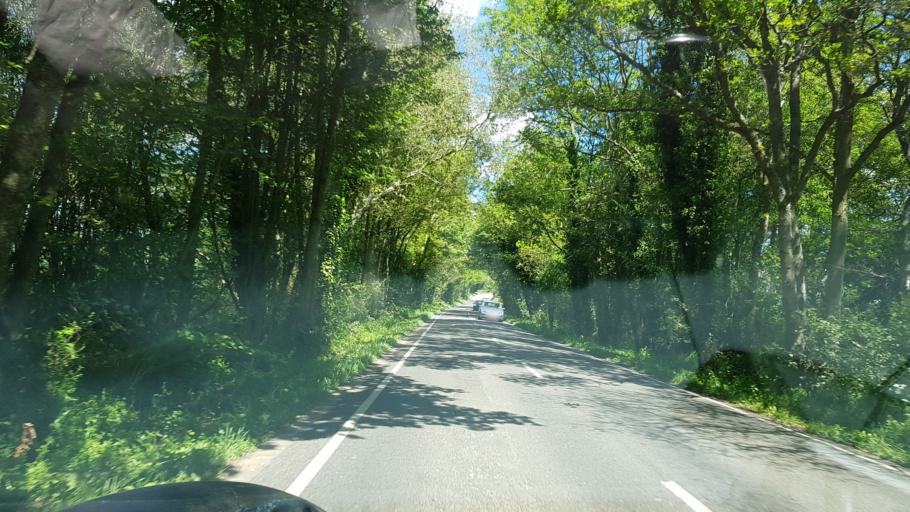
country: GB
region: England
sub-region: Surrey
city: Cranleigh
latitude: 51.1331
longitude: -0.5427
